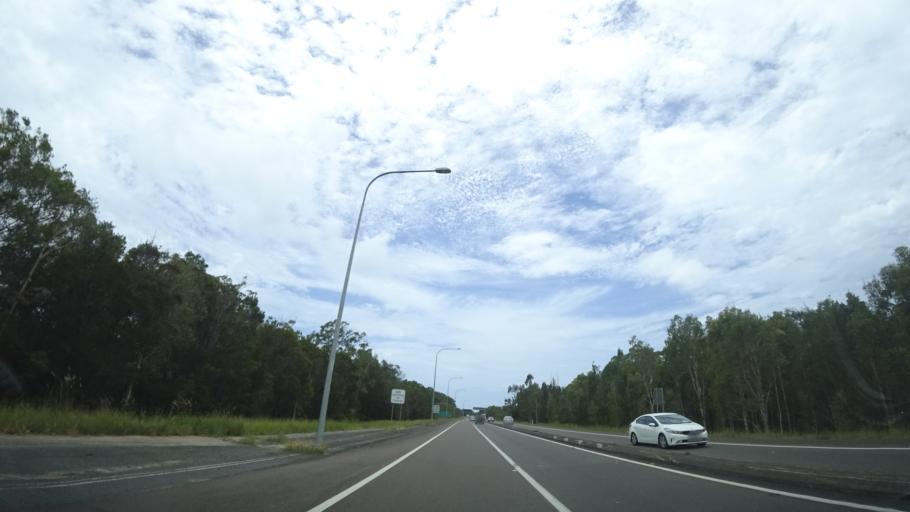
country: AU
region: Queensland
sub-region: Sunshine Coast
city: Mooloolaba
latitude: -26.7114
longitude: 153.0923
